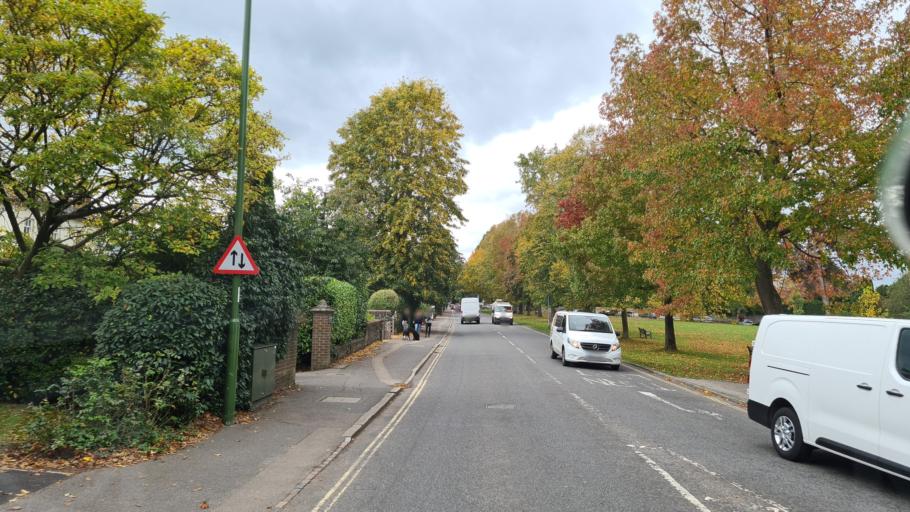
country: GB
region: England
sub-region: West Sussex
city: Haywards Heath
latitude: 50.9994
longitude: -0.1079
